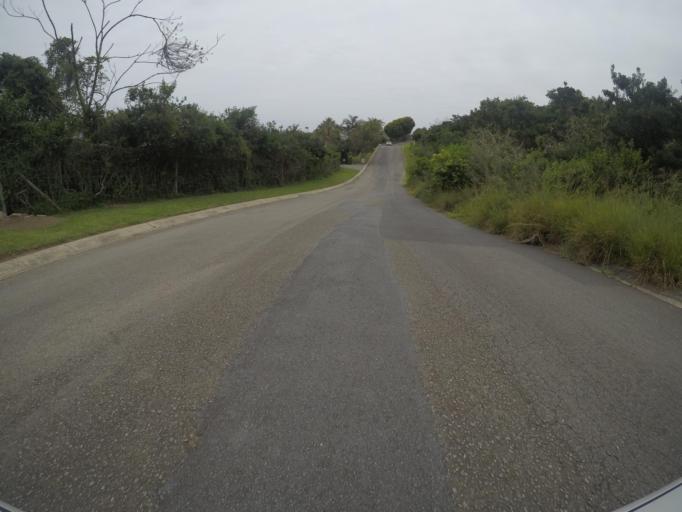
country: ZA
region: Eastern Cape
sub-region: Buffalo City Metropolitan Municipality
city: East London
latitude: -32.9794
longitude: 27.9380
